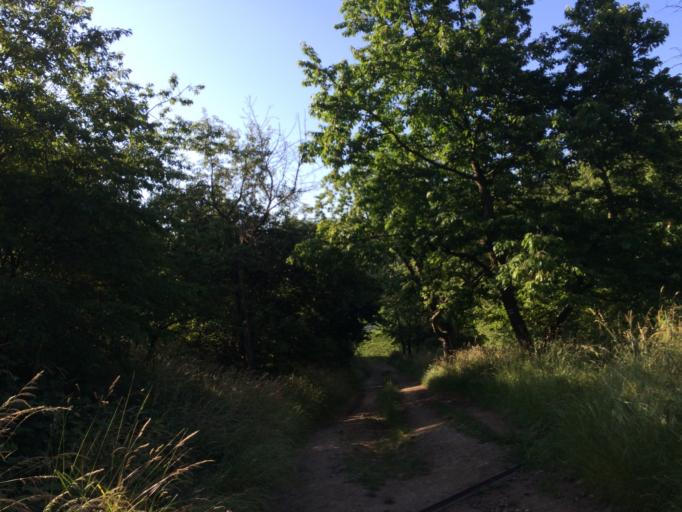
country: CZ
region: Central Bohemia
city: Horomerice
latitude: 50.0951
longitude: 14.3237
